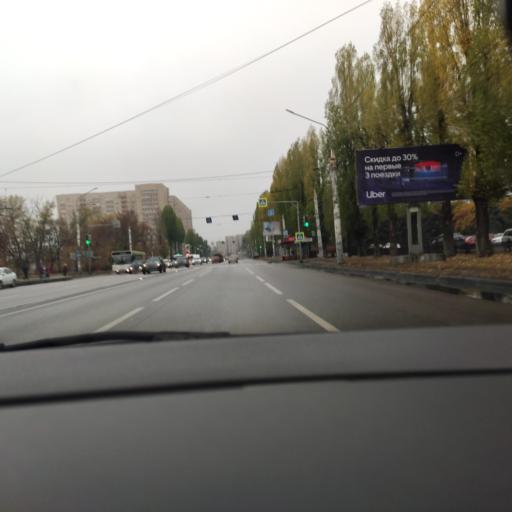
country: RU
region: Voronezj
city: Voronezh
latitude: 51.6771
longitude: 39.2581
